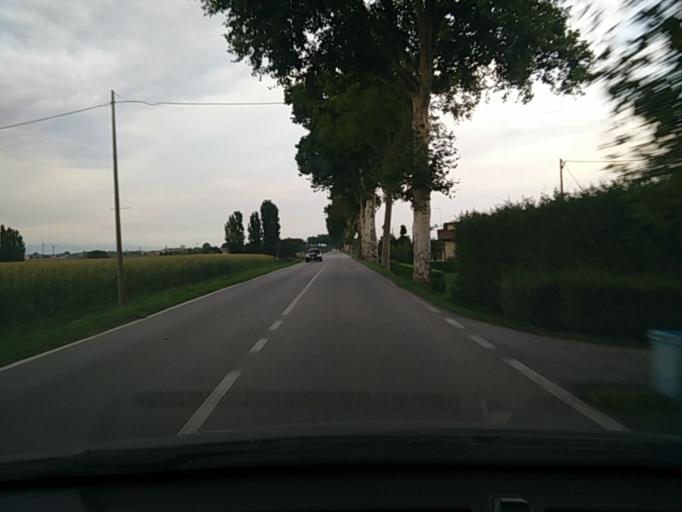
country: IT
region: Veneto
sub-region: Provincia di Venezia
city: Musile di Piave
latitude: 45.5977
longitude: 12.5581
